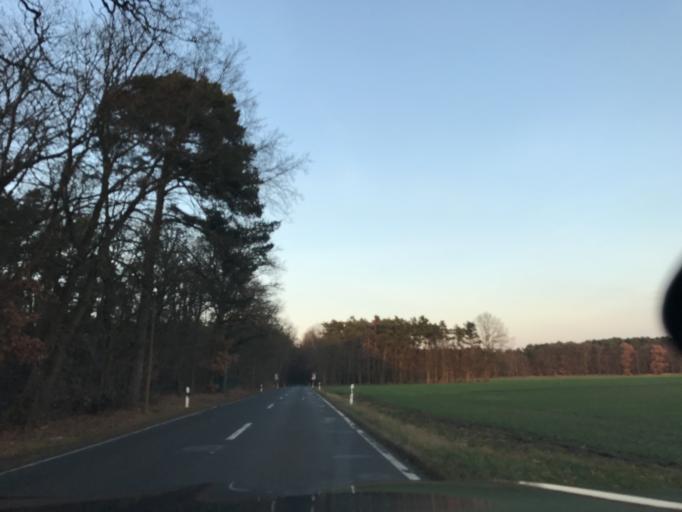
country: DE
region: Brandenburg
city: Wusterwitz
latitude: 52.4604
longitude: 12.4414
